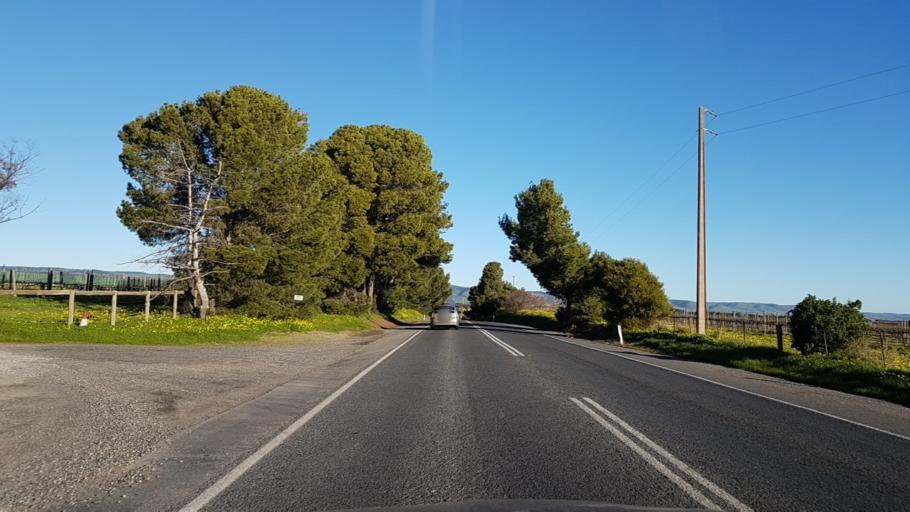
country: AU
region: South Australia
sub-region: Onkaparinga
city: Aldinga
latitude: -35.2378
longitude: 138.4937
